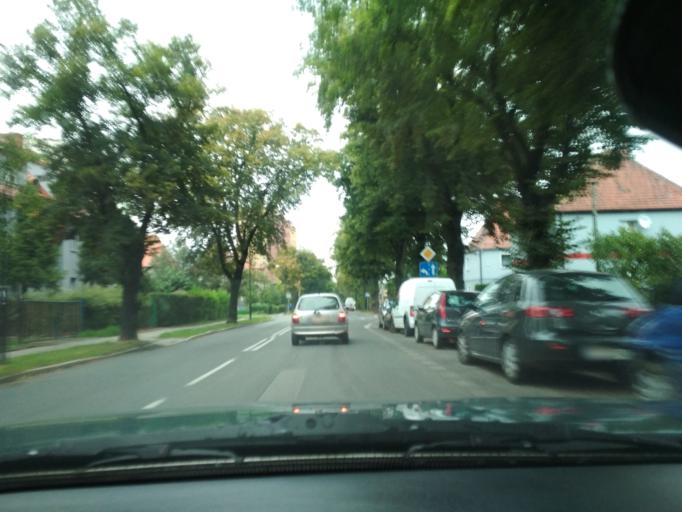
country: PL
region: Silesian Voivodeship
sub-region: Gliwice
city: Gliwice
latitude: 50.2805
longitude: 18.6751
